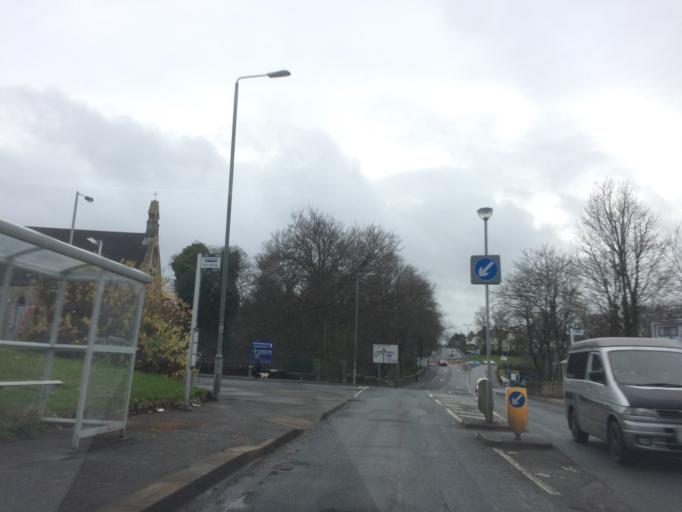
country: GB
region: Scotland
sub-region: East Renfrewshire
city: Giffnock
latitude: 55.8018
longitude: -4.3208
